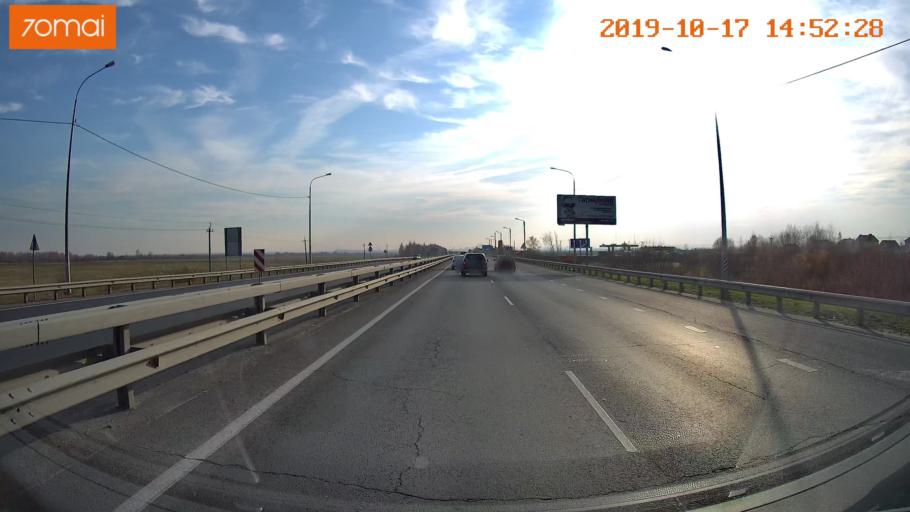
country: RU
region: Rjazan
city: Polyany
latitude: 54.7070
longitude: 39.8456
